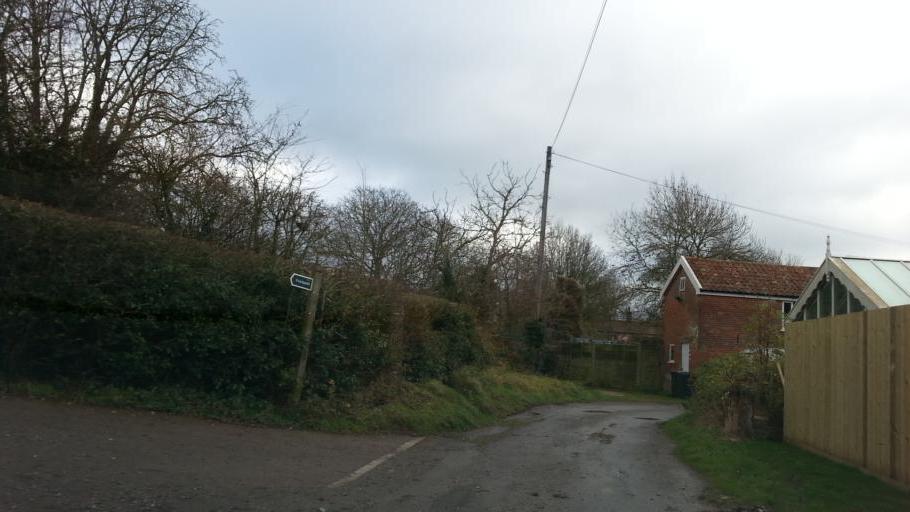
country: GB
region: England
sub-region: Suffolk
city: Cookley
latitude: 52.3033
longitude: 1.3670
